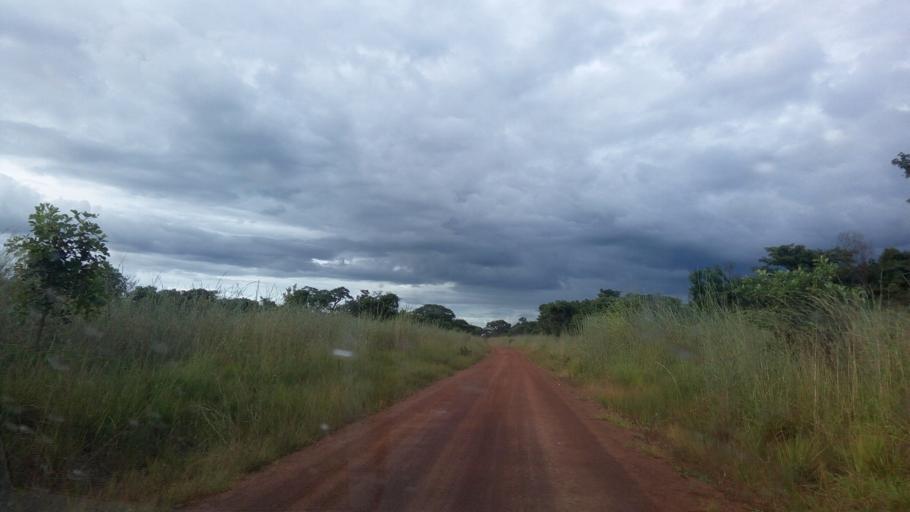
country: ZM
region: Luapula
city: Mwense
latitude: -10.3034
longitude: 28.1170
